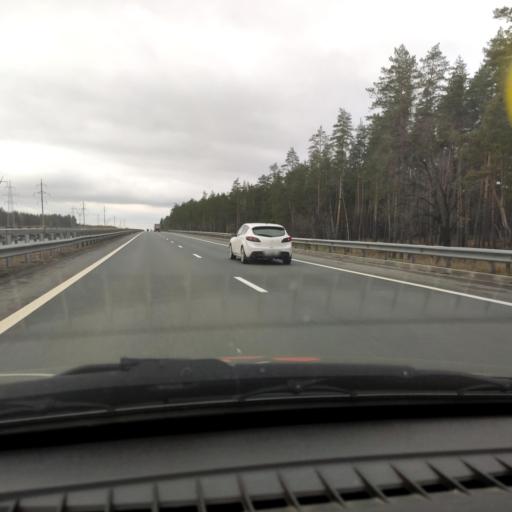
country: RU
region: Samara
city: Povolzhskiy
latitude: 53.5175
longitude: 49.7658
